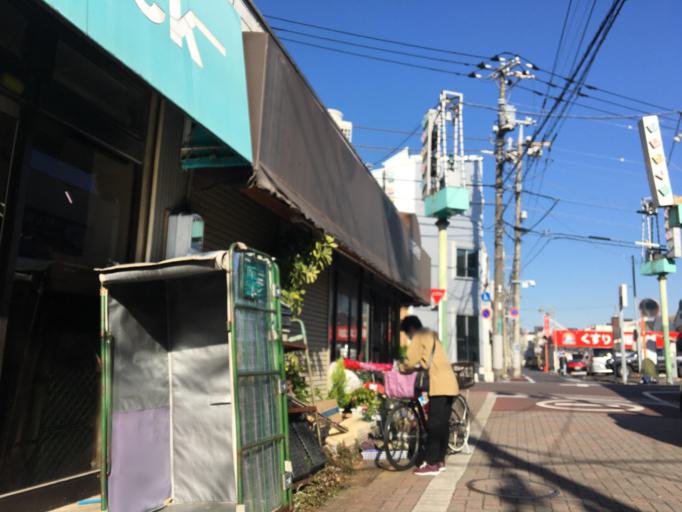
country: JP
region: Tokyo
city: Urayasu
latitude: 35.6875
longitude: 139.9033
